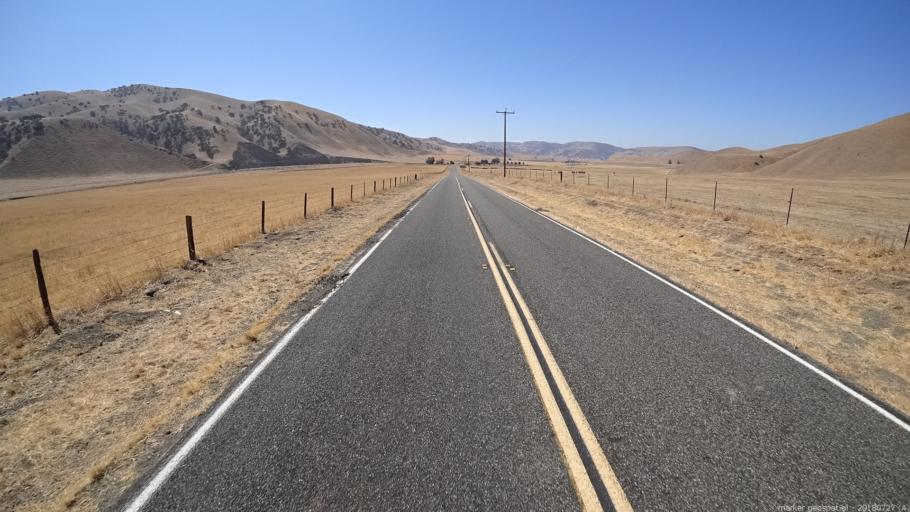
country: US
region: California
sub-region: Monterey County
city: King City
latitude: 36.3073
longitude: -120.9287
